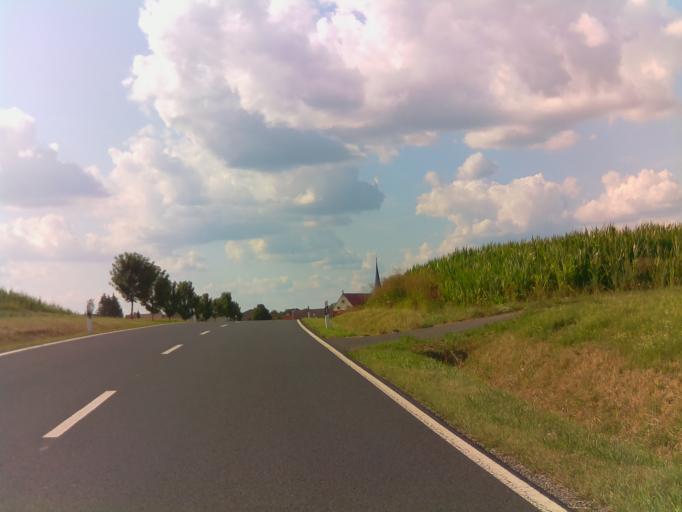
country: DE
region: Bavaria
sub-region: Regierungsbezirk Unterfranken
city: Bundorf
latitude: 50.2681
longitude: 10.5308
